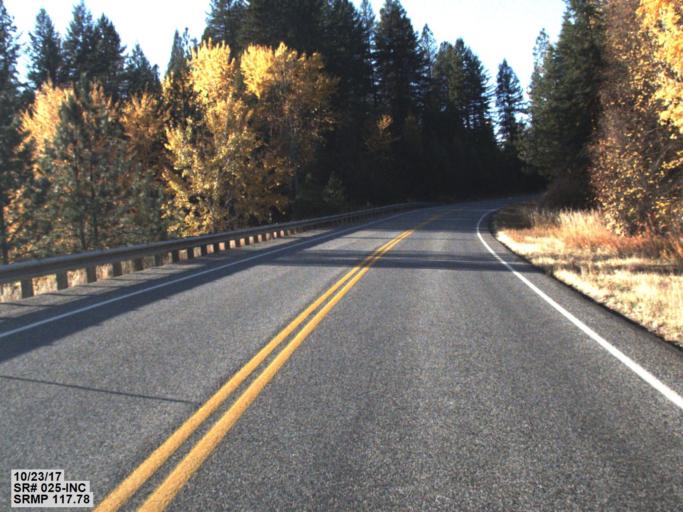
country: CA
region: British Columbia
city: Rossland
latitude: 48.9575
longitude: -117.7994
